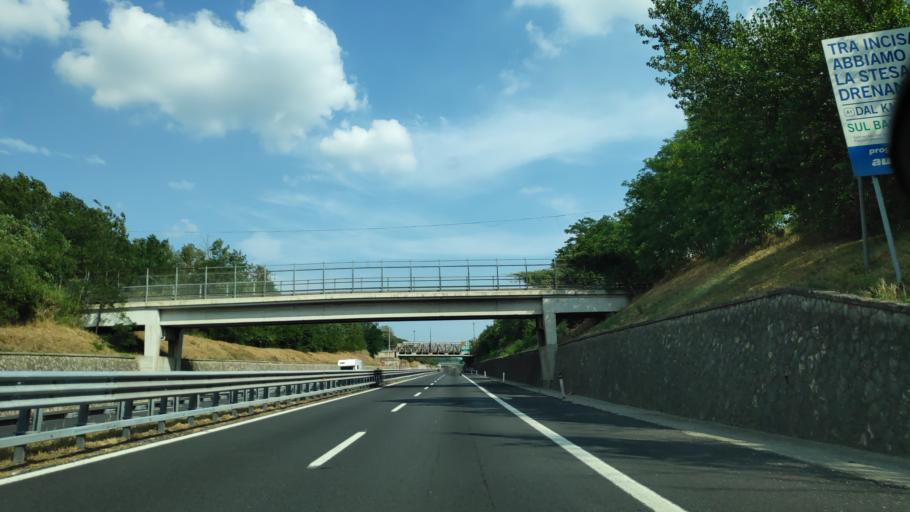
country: IT
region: Umbria
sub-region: Provincia di Terni
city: Attigliano
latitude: 42.5050
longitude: 12.3021
